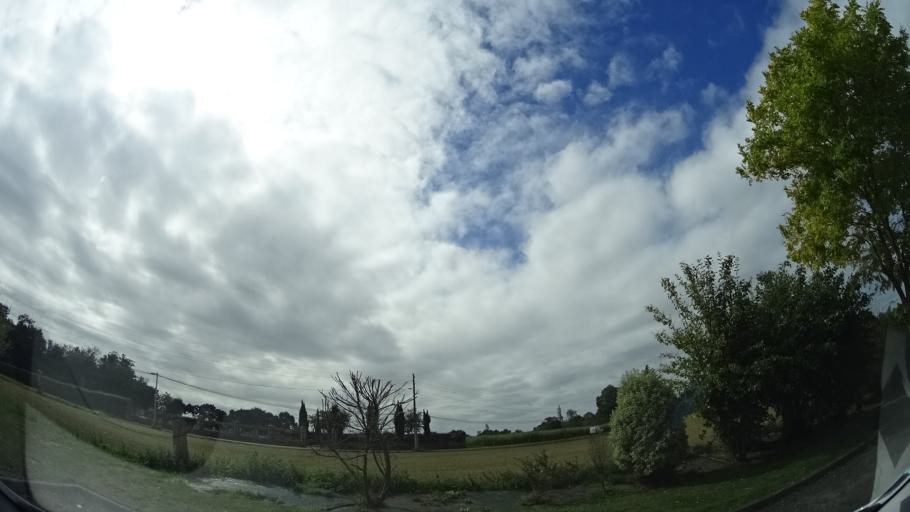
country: FR
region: Brittany
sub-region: Departement d'Ille-et-Vilaine
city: Tinteniac
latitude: 48.2697
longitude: -1.8567
